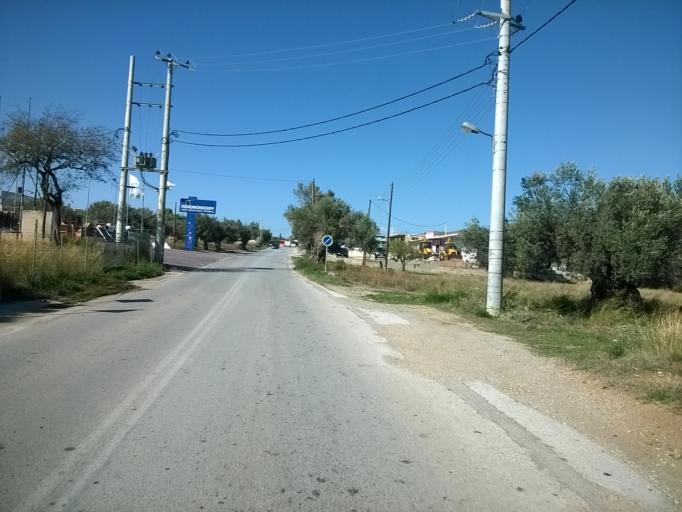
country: GR
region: Attica
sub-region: Nomarchia Anatolikis Attikis
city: Keratea
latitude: 37.8025
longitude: 23.9926
